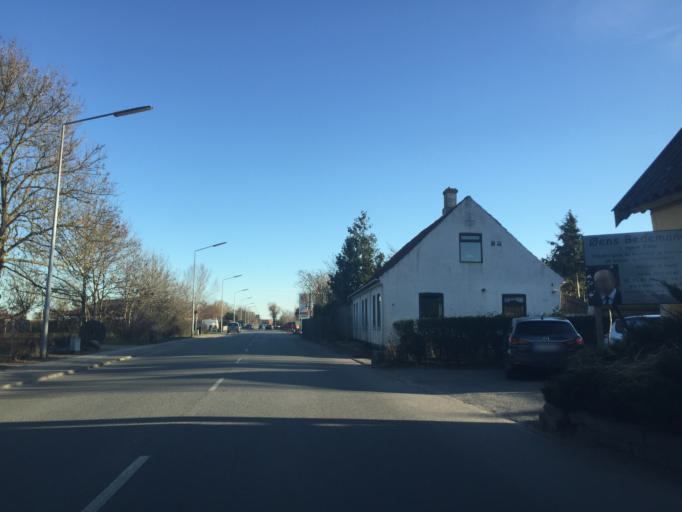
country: DK
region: Capital Region
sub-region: Dragor Kommune
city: Dragor
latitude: 55.5931
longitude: 12.6343
